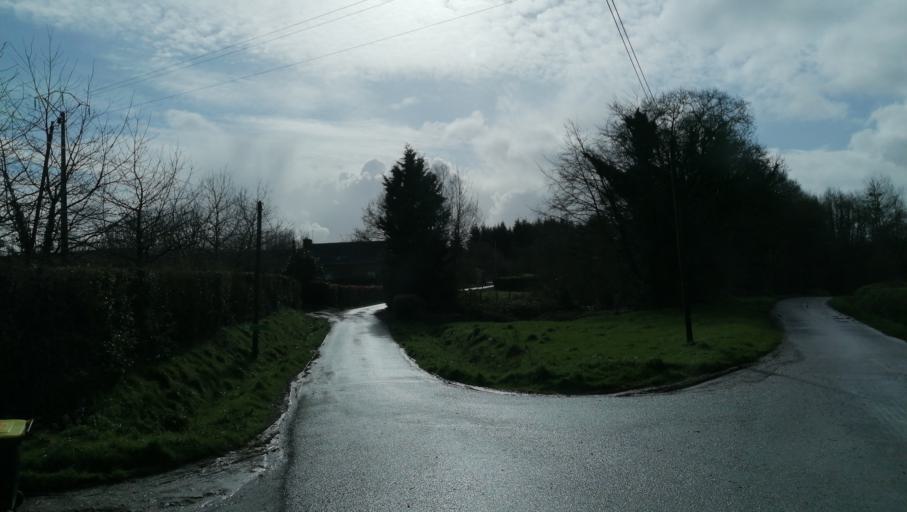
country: FR
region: Brittany
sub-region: Departement des Cotes-d'Armor
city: Lanrodec
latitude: 48.4988
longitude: -3.0266
